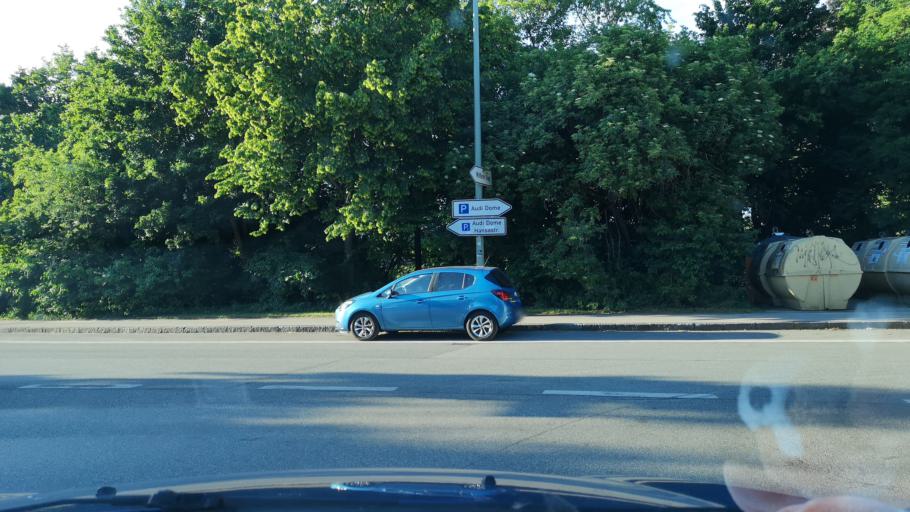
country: DE
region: Bavaria
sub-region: Upper Bavaria
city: Munich
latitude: 48.1280
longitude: 11.5205
